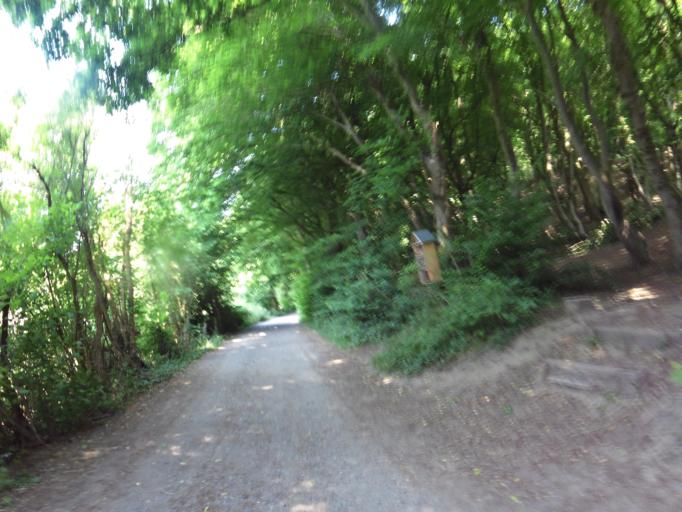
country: DE
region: North Rhine-Westphalia
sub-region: Regierungsbezirk Koln
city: Wurselen
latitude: 50.8187
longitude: 6.1090
